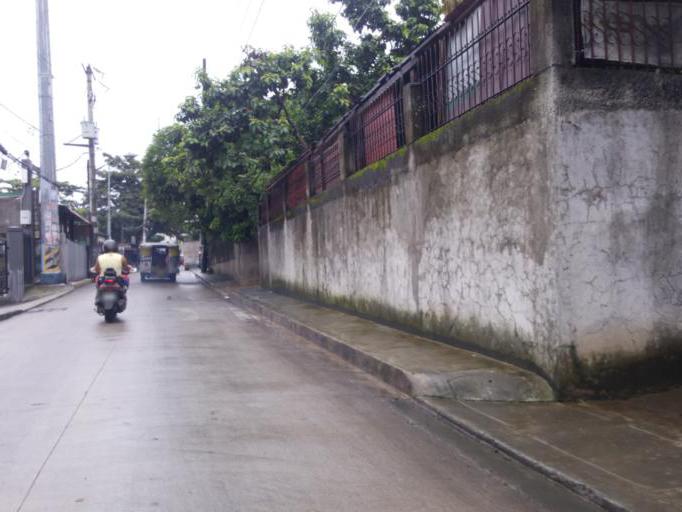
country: PH
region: Calabarzon
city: Bagong Pagasa
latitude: 14.7200
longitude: 121.0414
